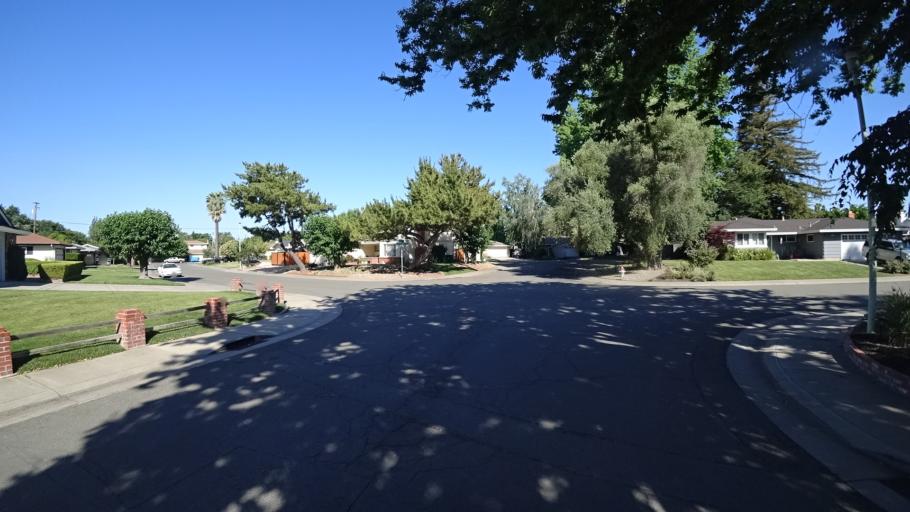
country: US
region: California
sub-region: Sacramento County
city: Rosemont
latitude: 38.5548
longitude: -121.3961
